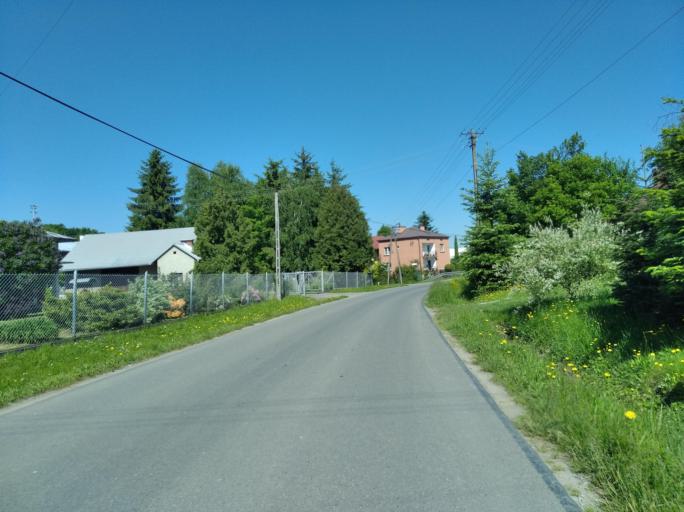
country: PL
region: Subcarpathian Voivodeship
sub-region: Powiat krosnienski
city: Korczyna
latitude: 49.7200
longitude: 21.7899
